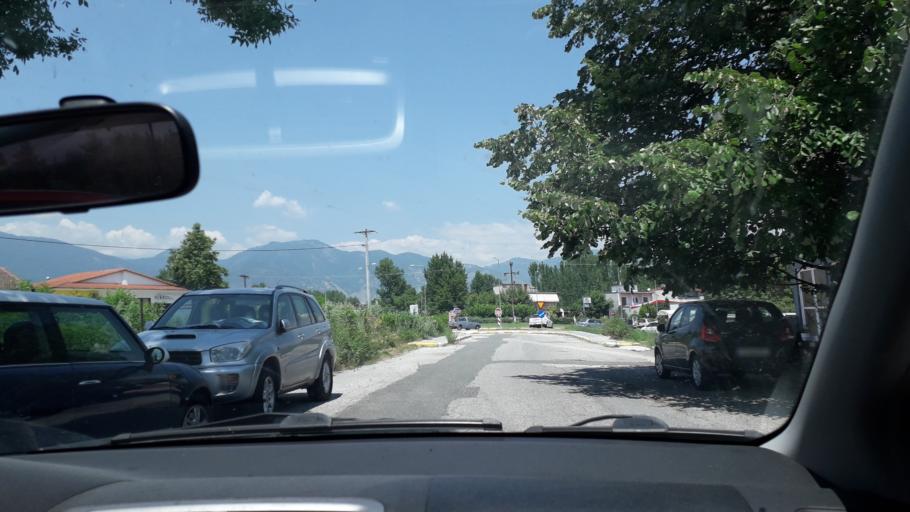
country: GR
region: Central Macedonia
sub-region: Nomos Pellis
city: Aridaia
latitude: 40.9687
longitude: 22.0561
